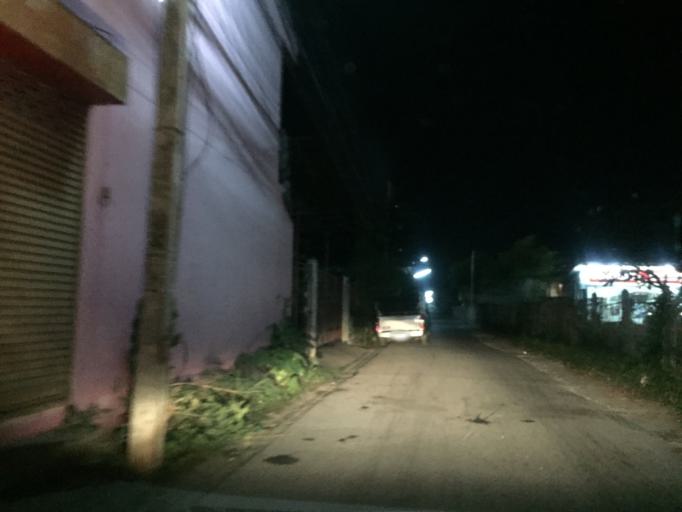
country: TH
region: Lamphun
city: Lamphun
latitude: 18.5703
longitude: 99.0052
